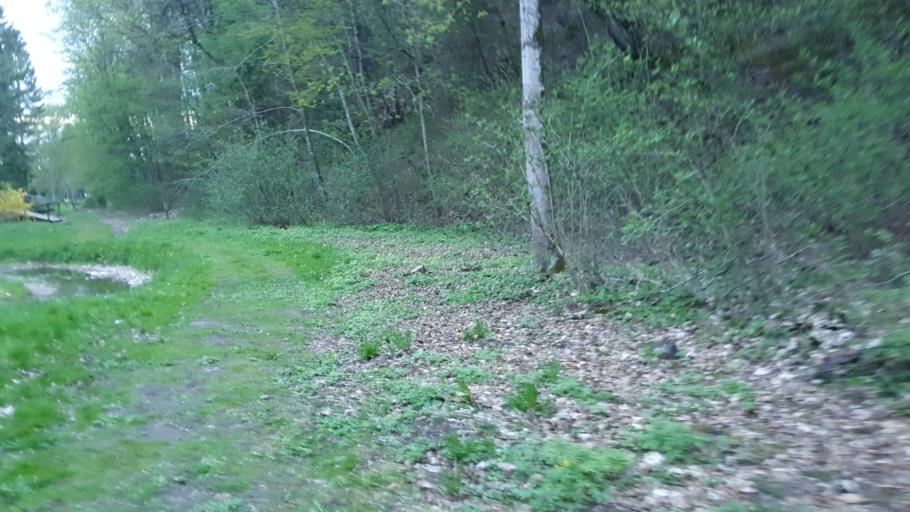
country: LT
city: Sakiai
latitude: 55.0795
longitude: 23.1787
